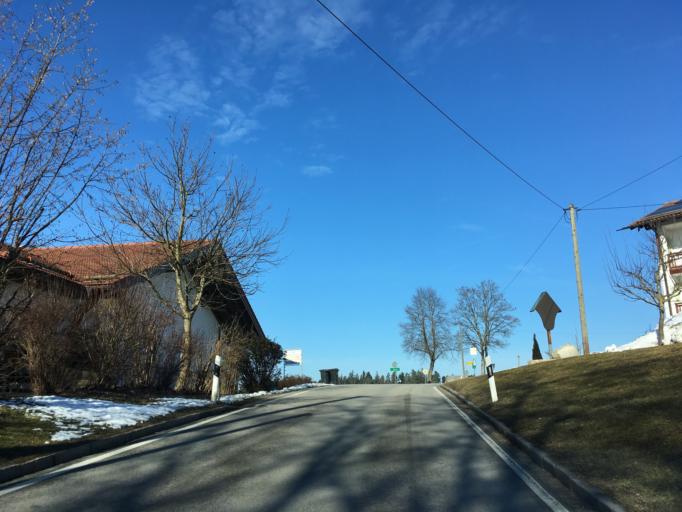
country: DE
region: Bavaria
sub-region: Upper Bavaria
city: Ramerberg
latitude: 48.0060
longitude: 12.1447
